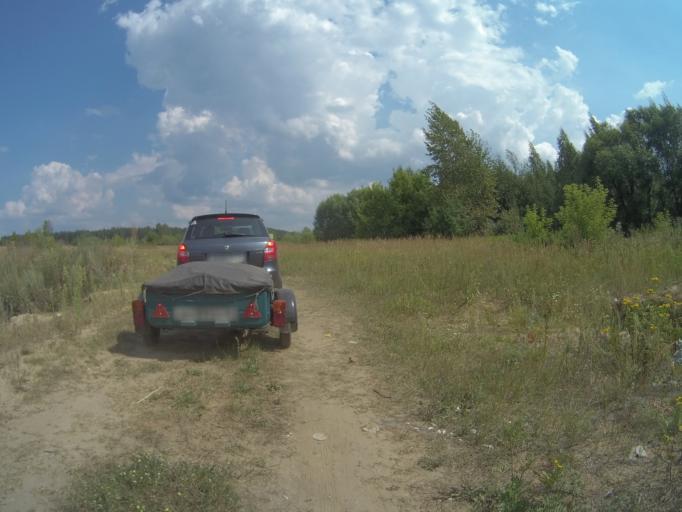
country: RU
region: Vladimir
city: Kideksha
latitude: 56.4247
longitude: 40.5420
